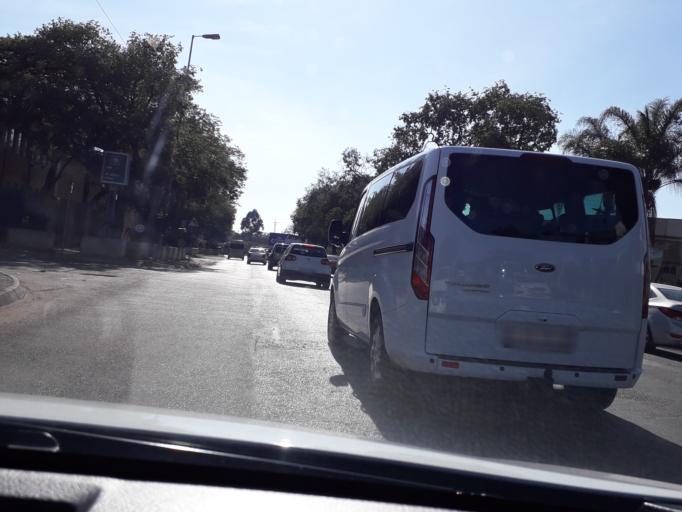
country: ZA
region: Gauteng
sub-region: City of Tshwane Metropolitan Municipality
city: Pretoria
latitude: -25.7457
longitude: 28.2419
